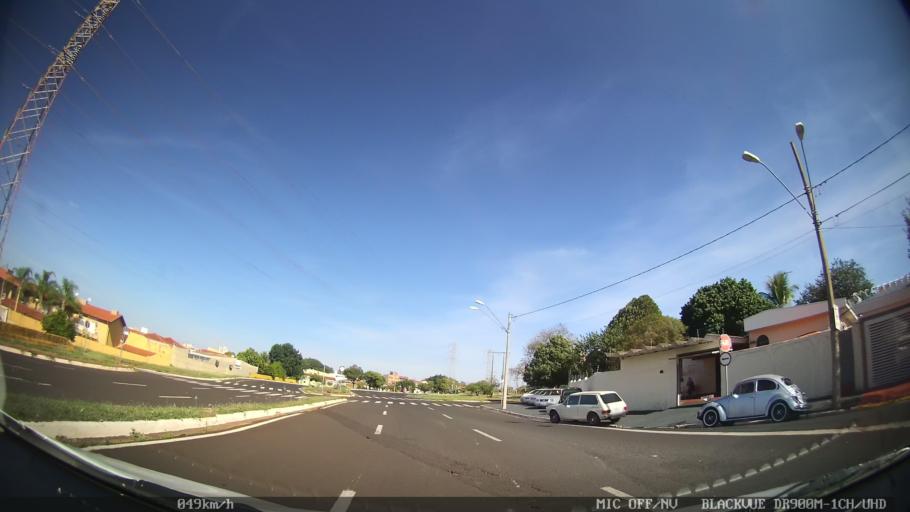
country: BR
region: Sao Paulo
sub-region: Ribeirao Preto
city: Ribeirao Preto
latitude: -21.1814
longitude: -47.7831
